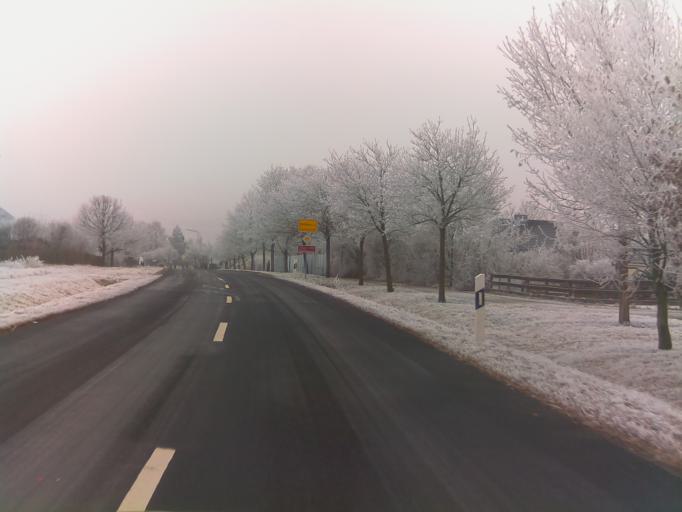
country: DE
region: Bavaria
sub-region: Regierungsbezirk Unterfranken
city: Sondheim vor der Rhoen
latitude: 50.4839
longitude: 10.1880
